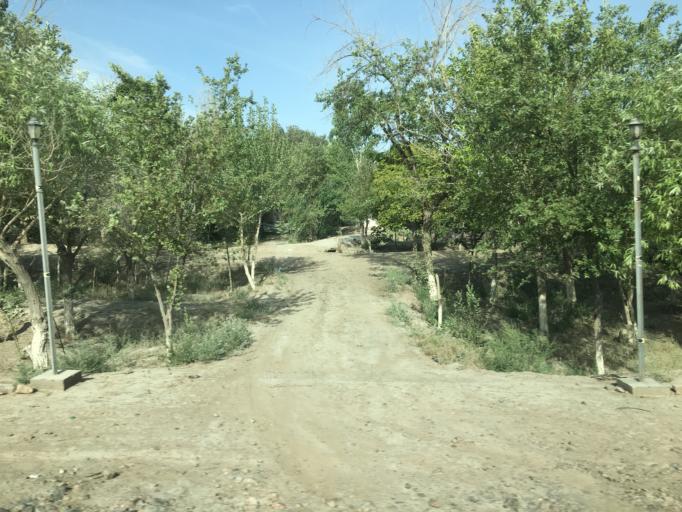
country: TM
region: Dasoguz
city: Dasoguz
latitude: 41.7807
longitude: 59.9541
